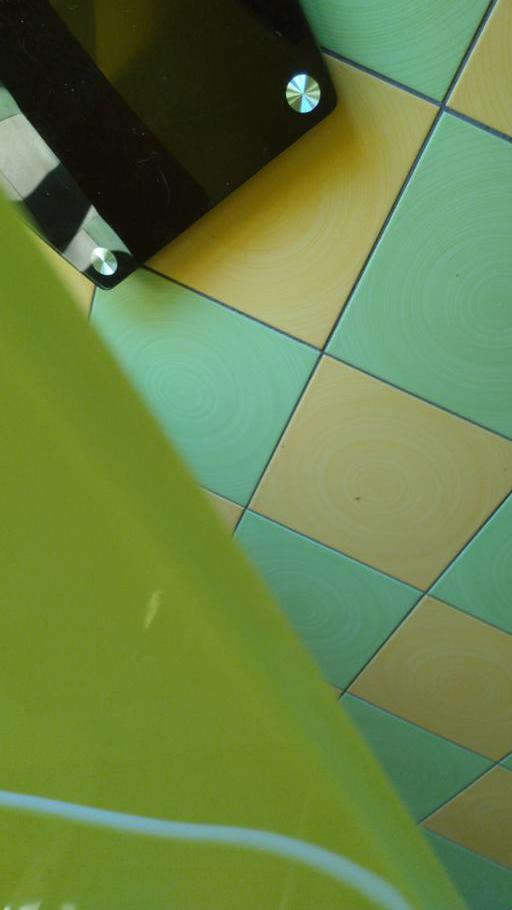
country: RU
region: Tverskaya
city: Krasnomayskiy
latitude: 57.5504
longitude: 34.3547
